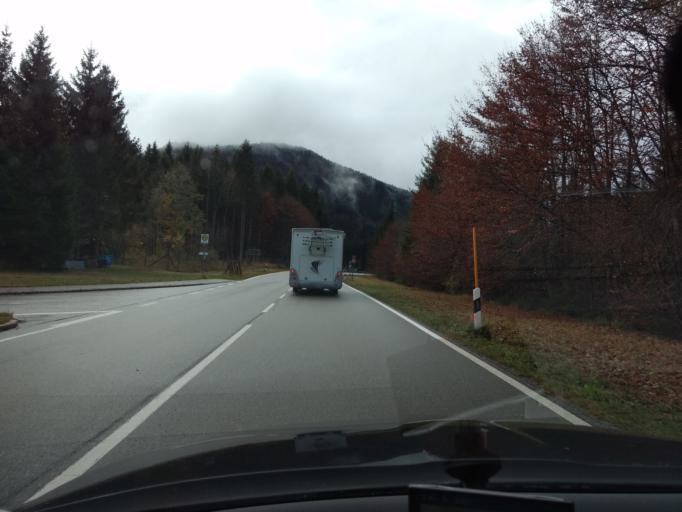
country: DE
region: Bavaria
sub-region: Upper Bavaria
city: Jachenau
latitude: 47.5704
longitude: 11.5303
